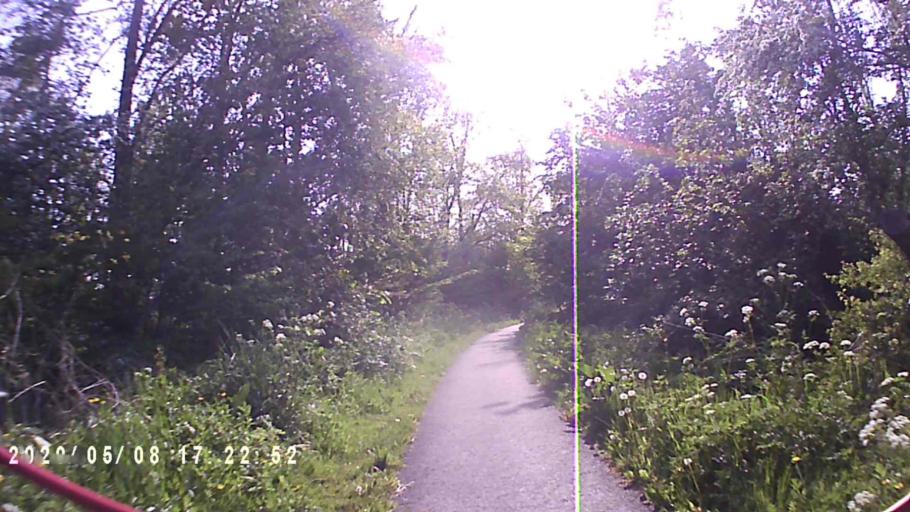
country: NL
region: Groningen
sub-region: Gemeente Winsum
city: Winsum
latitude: 53.3818
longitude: 6.5514
